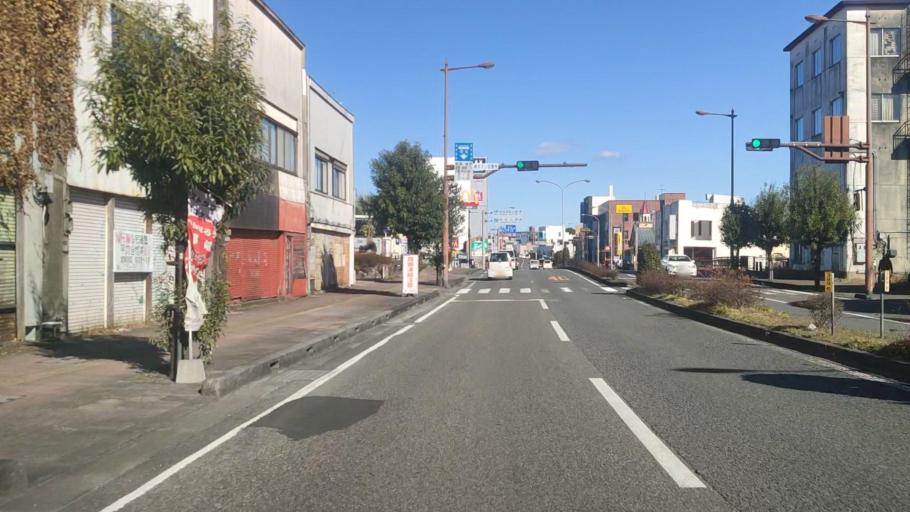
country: JP
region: Miyazaki
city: Miyakonojo
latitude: 31.7279
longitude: 131.0655
